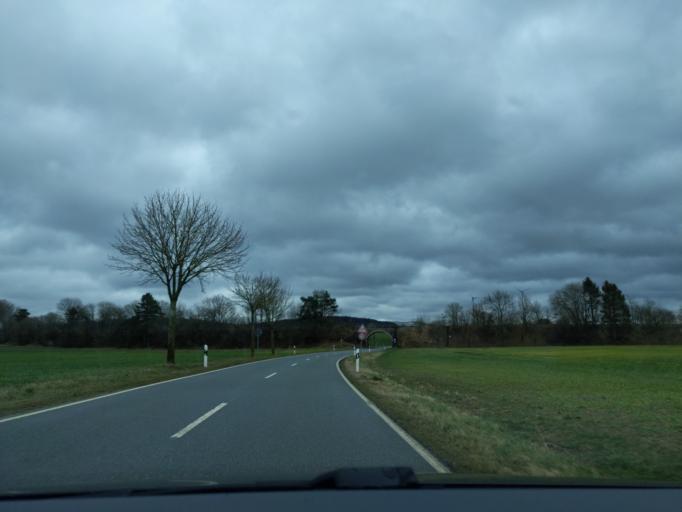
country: DE
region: Hesse
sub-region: Regierungsbezirk Kassel
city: Sachsenhausen
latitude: 51.2755
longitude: 8.9733
